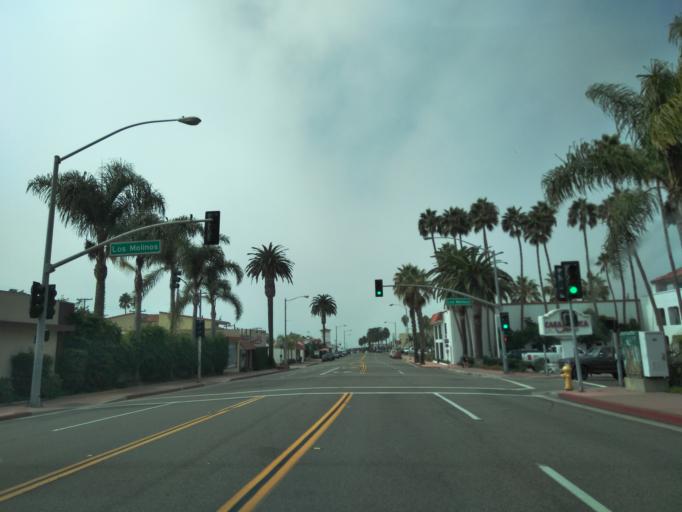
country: US
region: California
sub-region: Orange County
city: San Clemente
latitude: 33.4324
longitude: -117.6275
